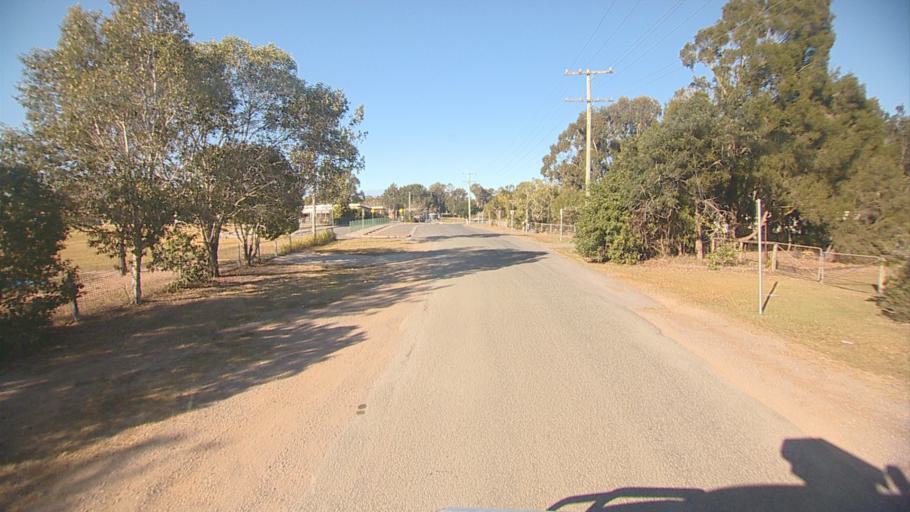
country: AU
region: Queensland
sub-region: Logan
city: Chambers Flat
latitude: -27.7630
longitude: 153.1051
